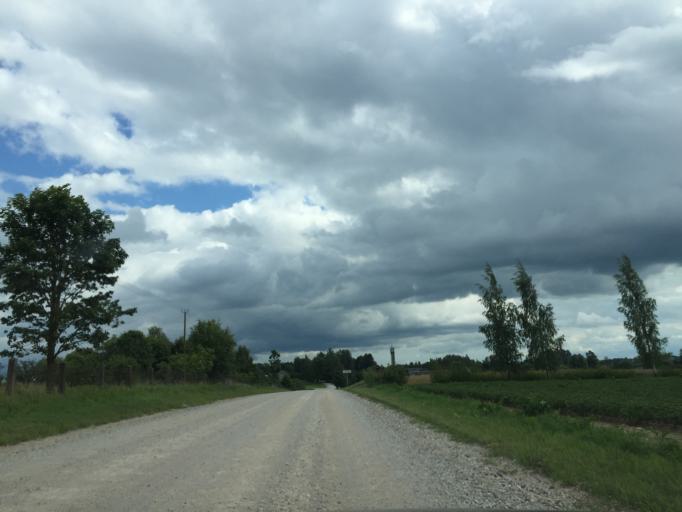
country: LV
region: Malpils
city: Malpils
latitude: 56.8642
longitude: 25.0141
